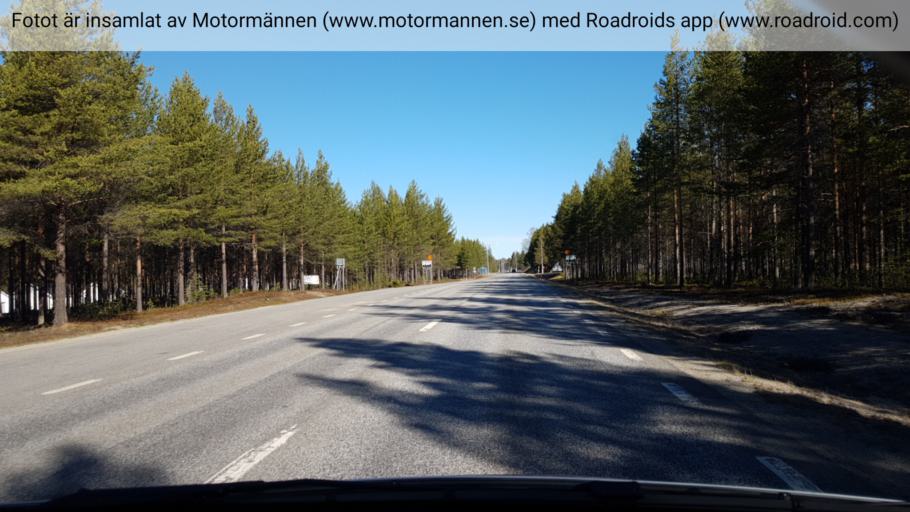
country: SE
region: Vaesterbotten
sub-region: Lycksele Kommun
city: Lycksele
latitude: 64.5736
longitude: 18.7123
